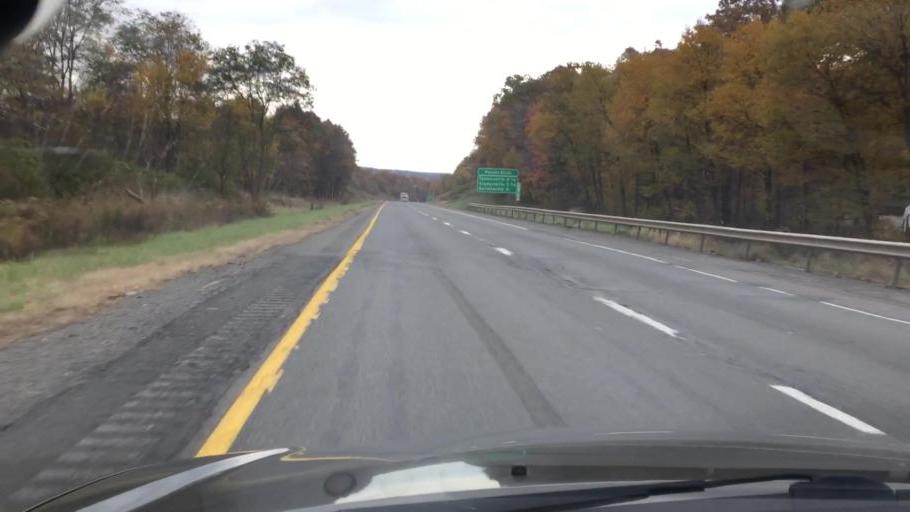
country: US
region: Pennsylvania
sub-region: Monroe County
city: Tannersville
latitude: 41.0625
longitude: -75.3388
